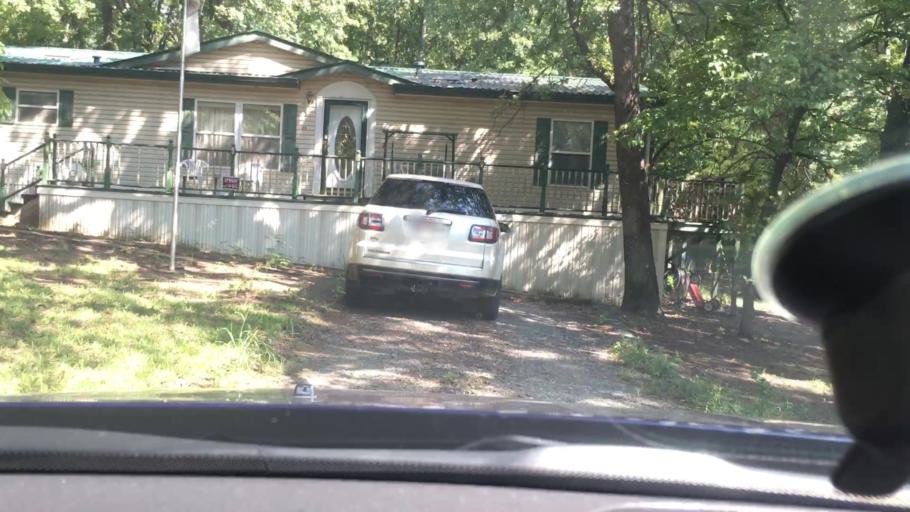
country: US
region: Texas
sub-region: Grayson County
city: Preston
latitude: 33.8908
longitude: -96.5651
